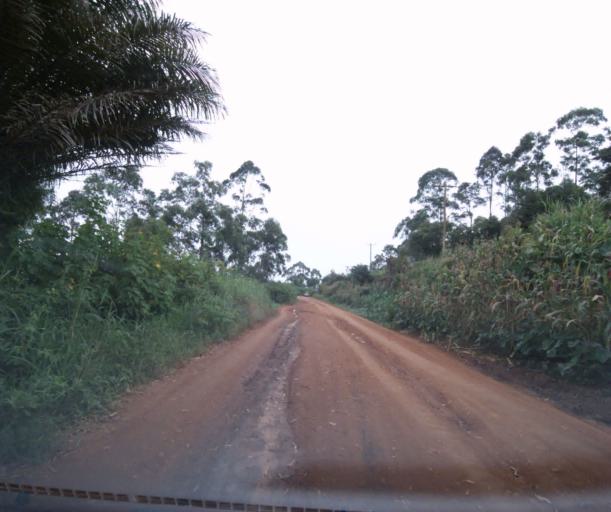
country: CM
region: West
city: Dschang
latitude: 5.5110
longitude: 9.9881
